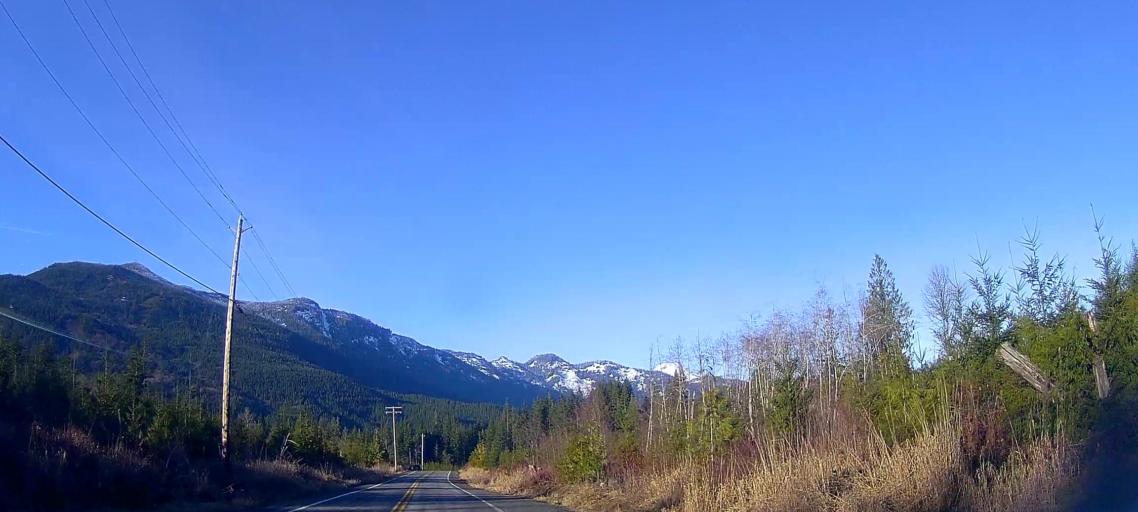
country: US
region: Washington
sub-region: Snohomish County
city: Darrington
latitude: 48.5689
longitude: -121.7678
